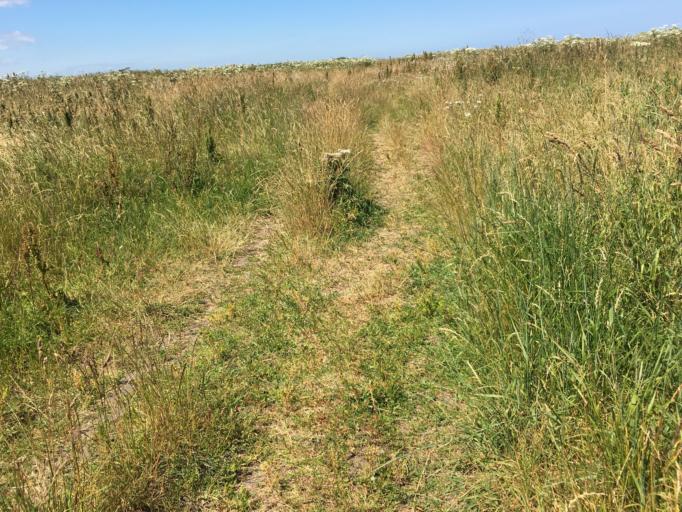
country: GB
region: England
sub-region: Northumberland
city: Ancroft
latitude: 55.7153
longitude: -1.9367
